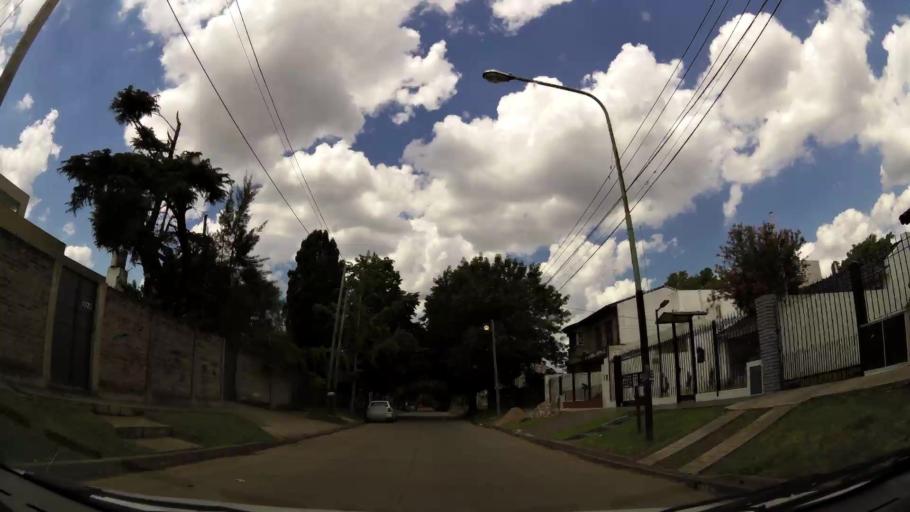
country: AR
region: Buenos Aires
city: Ituzaingo
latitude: -34.6549
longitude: -58.6773
